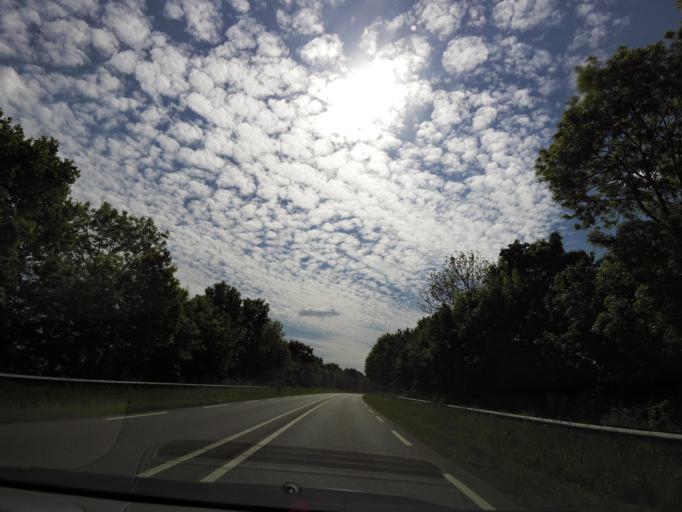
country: NL
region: Limburg
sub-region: Gemeente Roerdalen
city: Posterholt
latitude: 51.1146
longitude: 6.0410
